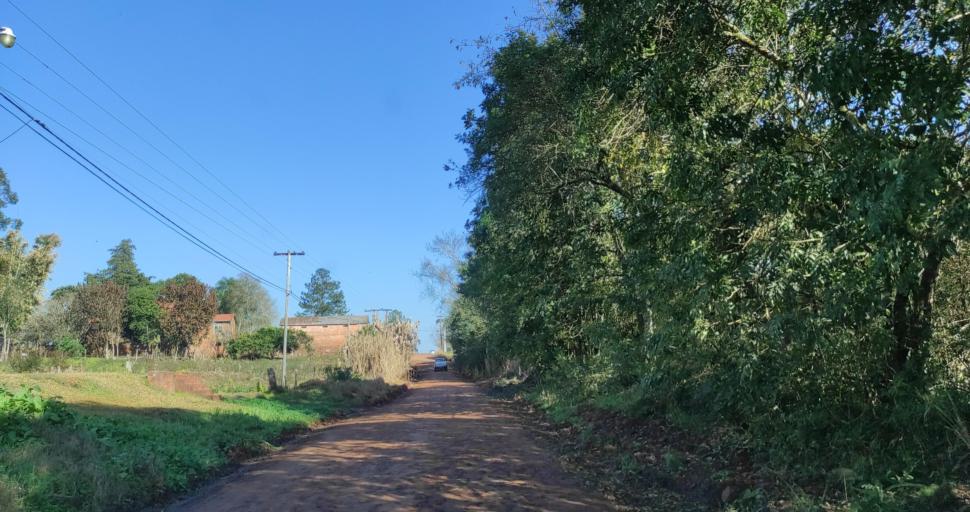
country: AR
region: Misiones
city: Capiovi
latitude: -26.8645
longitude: -55.0420
